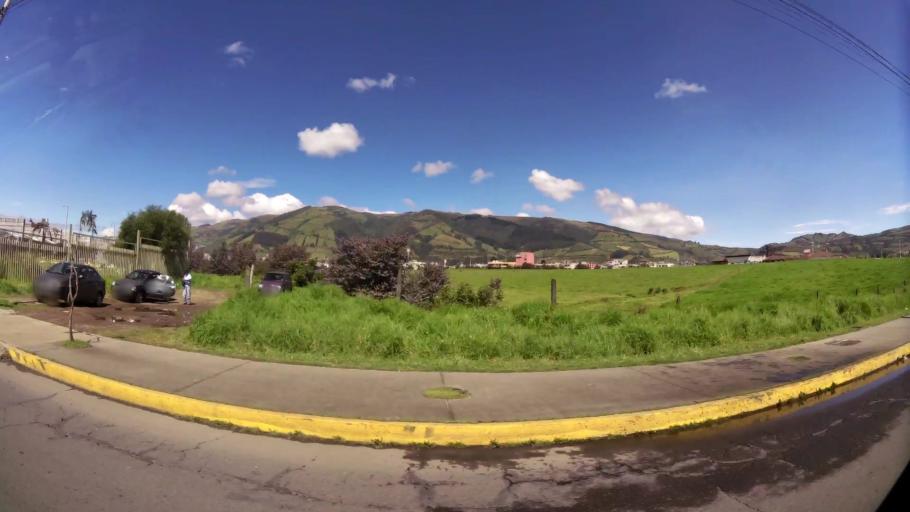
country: EC
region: Pichincha
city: Quito
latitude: -0.2933
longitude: -78.5560
